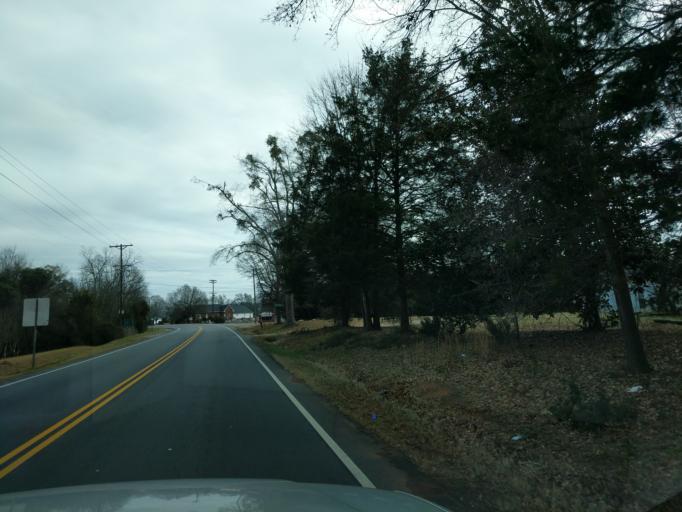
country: US
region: South Carolina
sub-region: Oconee County
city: Utica
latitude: 34.5665
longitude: -82.9051
